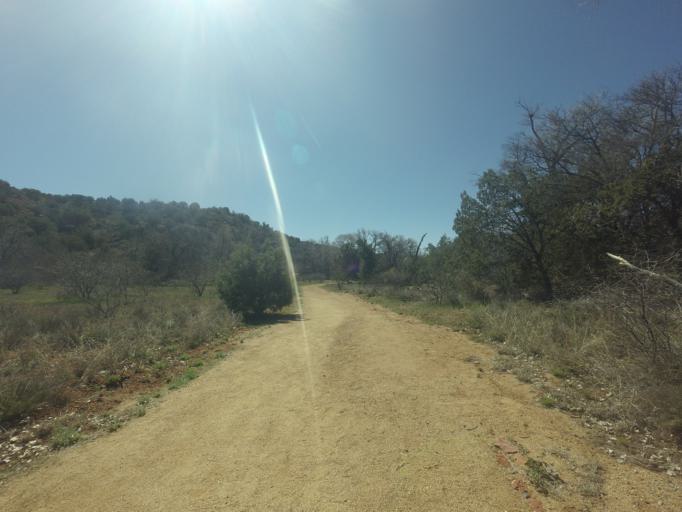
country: US
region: Arizona
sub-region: Yavapai County
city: Lake Montezuma
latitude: 34.6622
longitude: -111.7187
